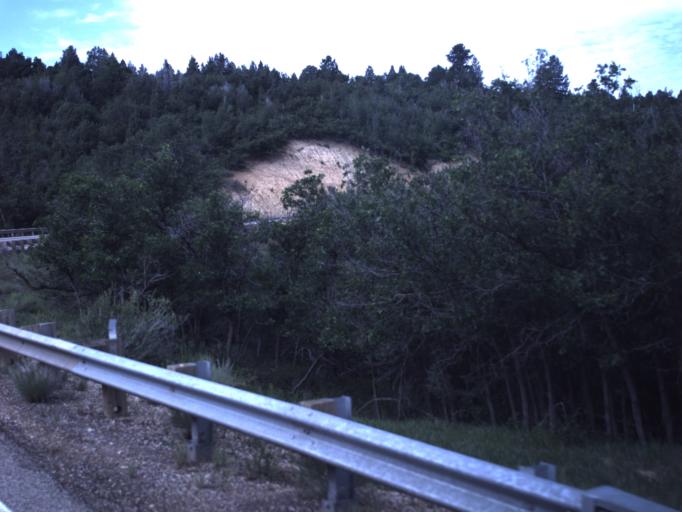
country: US
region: Utah
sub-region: Garfield County
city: Panguitch
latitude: 37.4897
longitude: -112.5242
